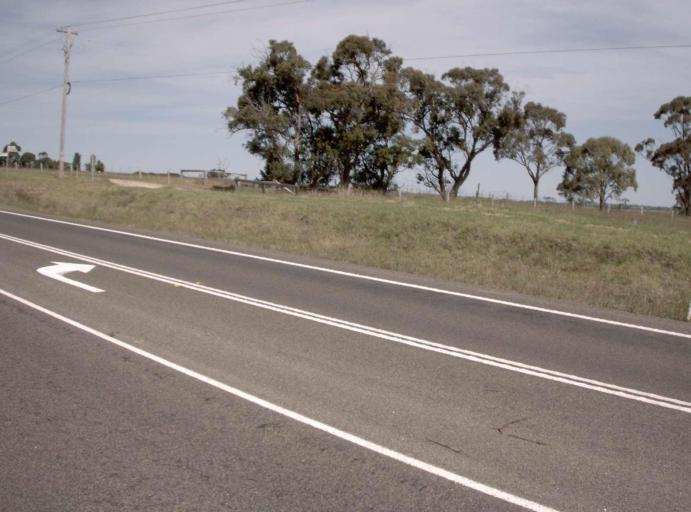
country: AU
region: Victoria
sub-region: East Gippsland
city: Lakes Entrance
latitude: -37.8225
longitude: 147.8040
